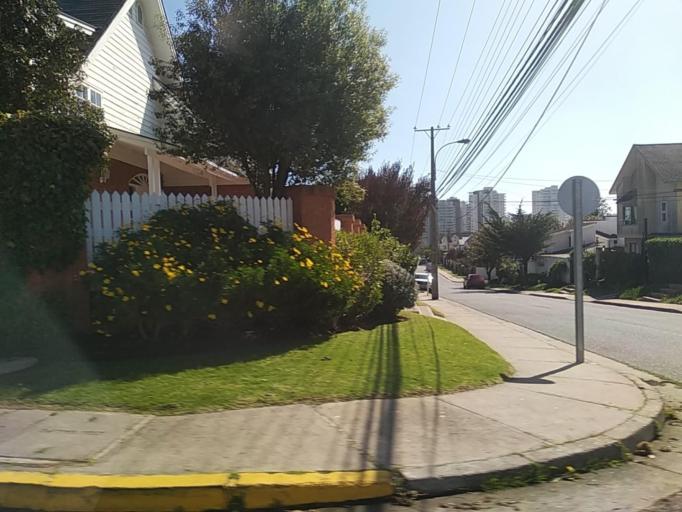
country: CL
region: Valparaiso
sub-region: Provincia de Valparaiso
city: Vina del Mar
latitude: -32.9393
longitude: -71.5425
